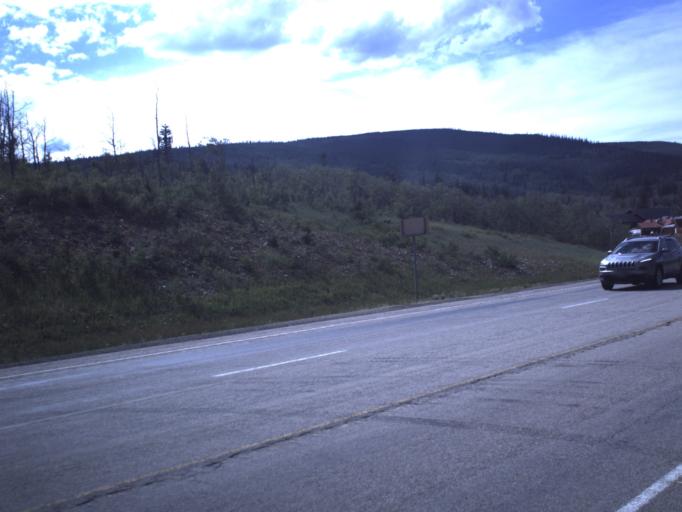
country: US
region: Utah
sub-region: Wasatch County
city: Heber
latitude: 40.2992
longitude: -111.2533
